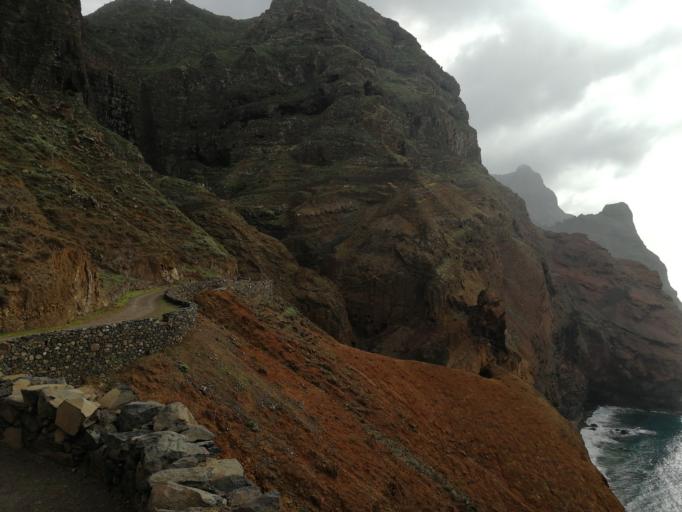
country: CV
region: Ribeira Grande
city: Ponta do Sol
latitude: 17.1962
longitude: -25.0962
